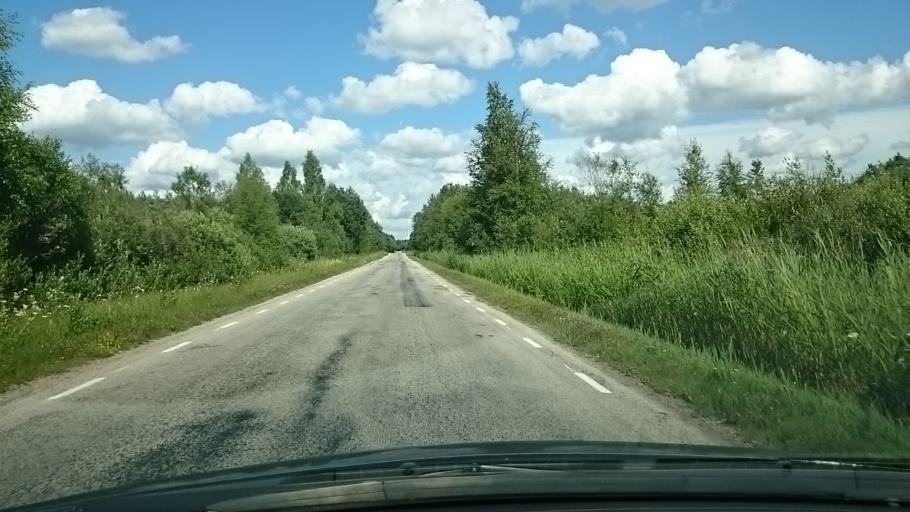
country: EE
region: Laeaene
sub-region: Haapsalu linn
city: Haapsalu
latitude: 59.0604
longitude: 23.5653
